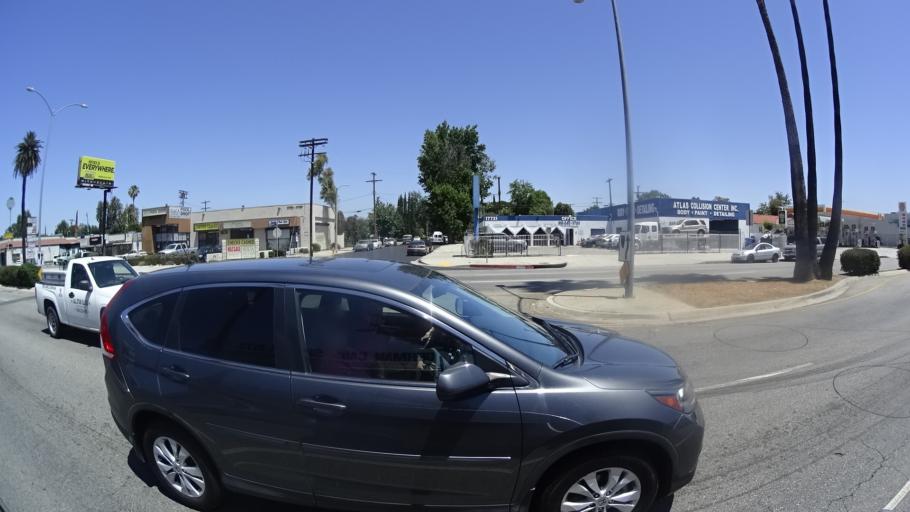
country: US
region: California
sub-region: Los Angeles County
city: Northridge
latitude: 34.2009
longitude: -118.5197
